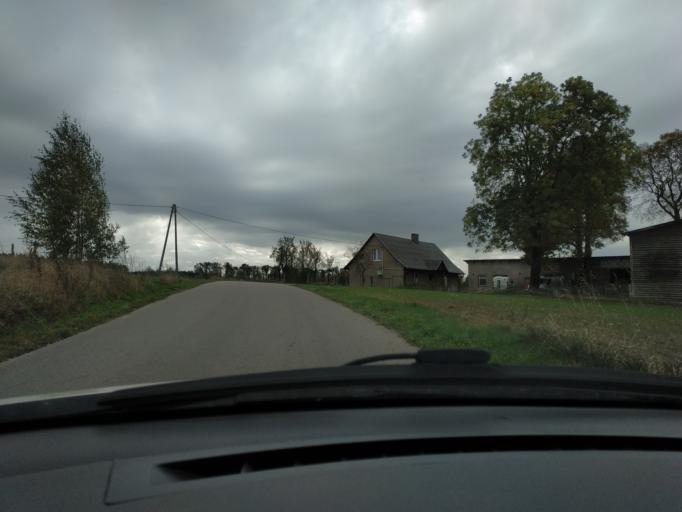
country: PL
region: Warmian-Masurian Voivodeship
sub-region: Powiat nowomiejski
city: Biskupiec
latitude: 53.4602
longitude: 19.3180
